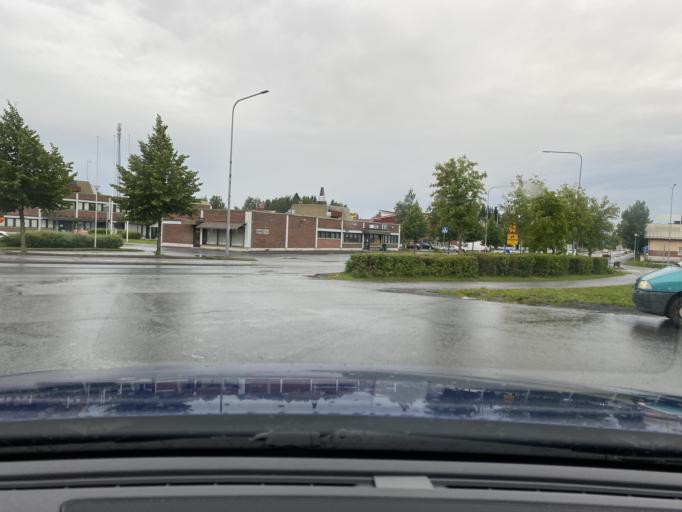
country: FI
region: Ostrobothnia
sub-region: Kyroenmaa
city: Laihia
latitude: 62.9783
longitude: 22.0113
